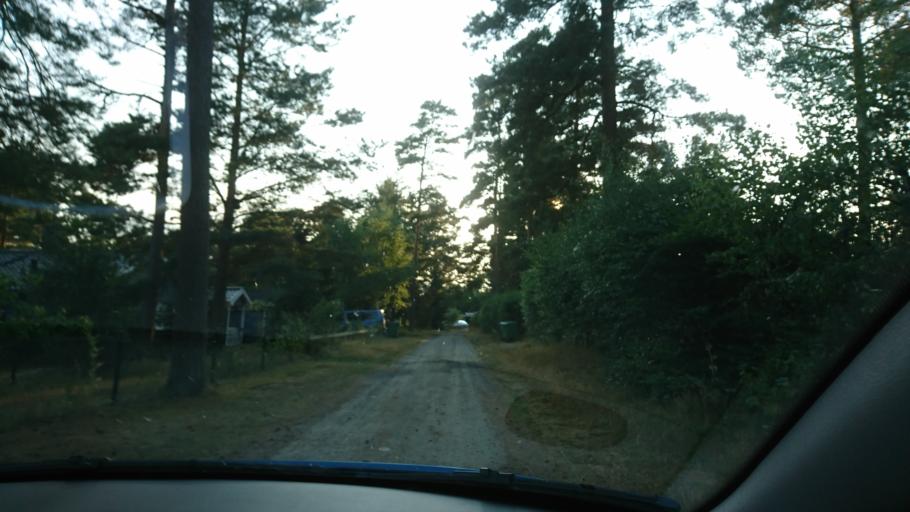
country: SE
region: Skane
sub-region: Simrishamns Kommun
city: Kivik
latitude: 55.7116
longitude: 14.1740
